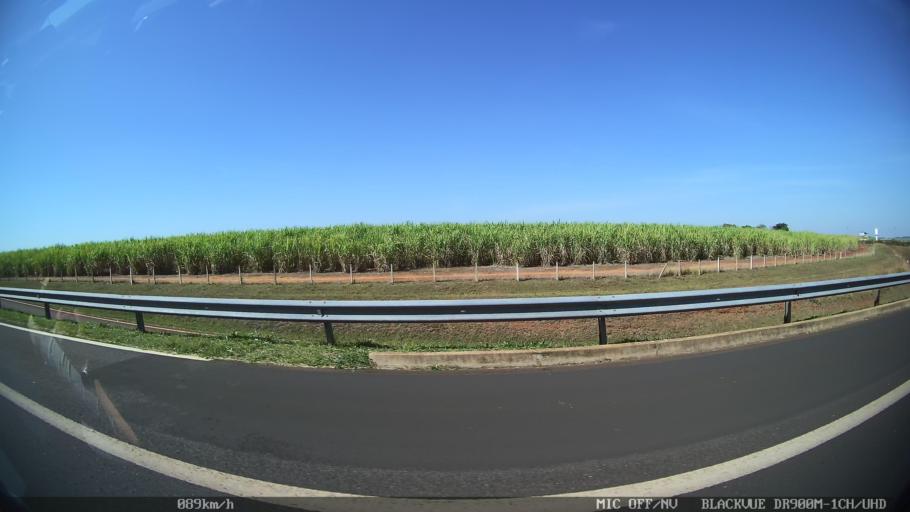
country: BR
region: Sao Paulo
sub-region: Batatais
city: Batatais
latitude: -20.8283
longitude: -47.5963
